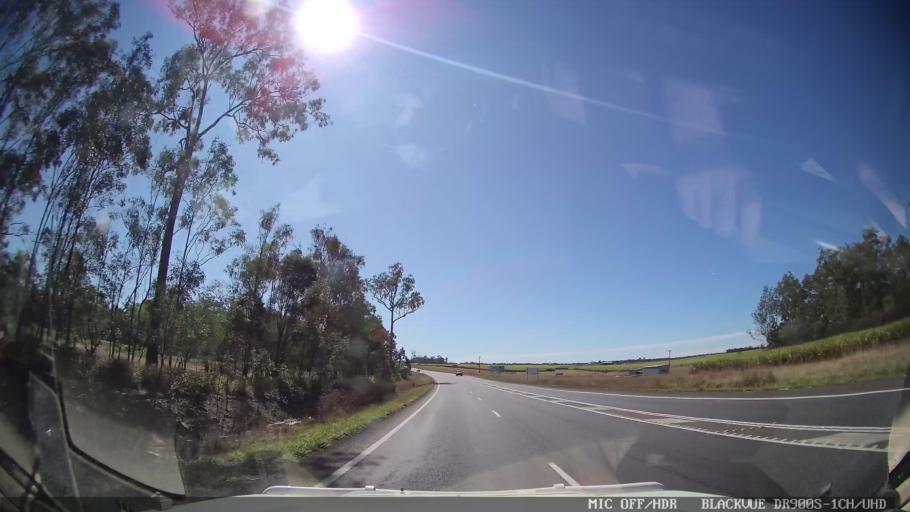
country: AU
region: Queensland
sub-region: Fraser Coast
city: Maryborough
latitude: -25.6461
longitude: 152.6369
